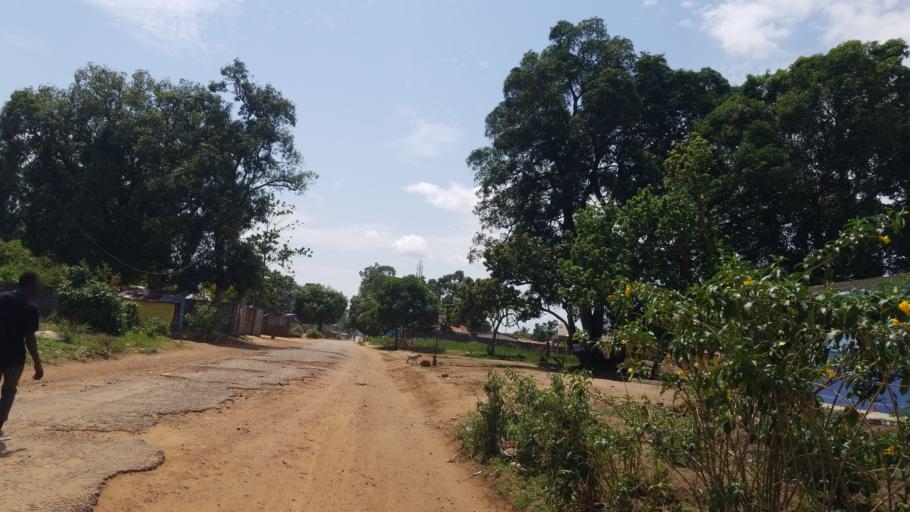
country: SL
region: Western Area
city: Waterloo
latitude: 8.3107
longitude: -13.0535
